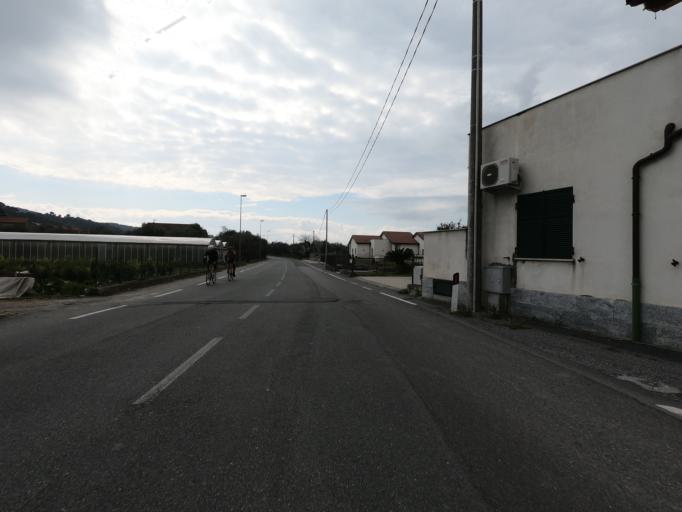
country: IT
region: Liguria
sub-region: Provincia di Savona
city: Andora
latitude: 43.9765
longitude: 8.1359
